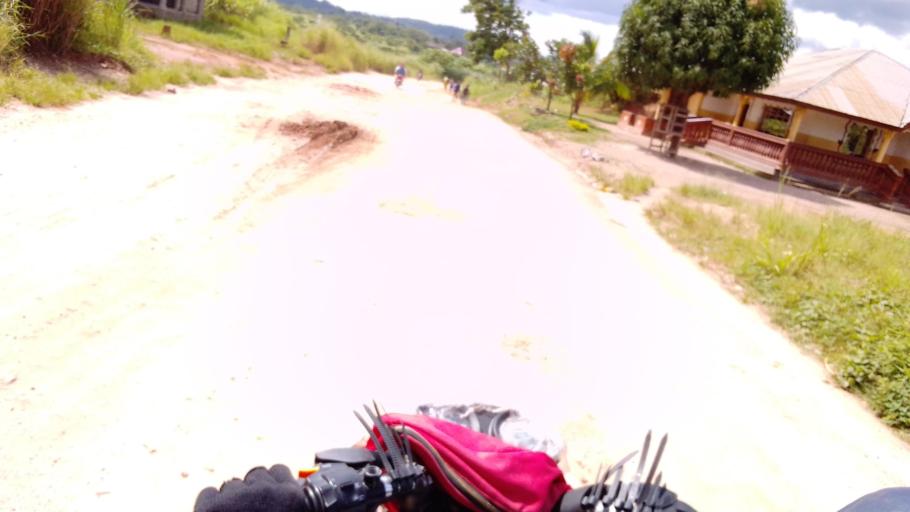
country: SL
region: Eastern Province
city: Koidu
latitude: 8.6699
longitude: -10.9791
